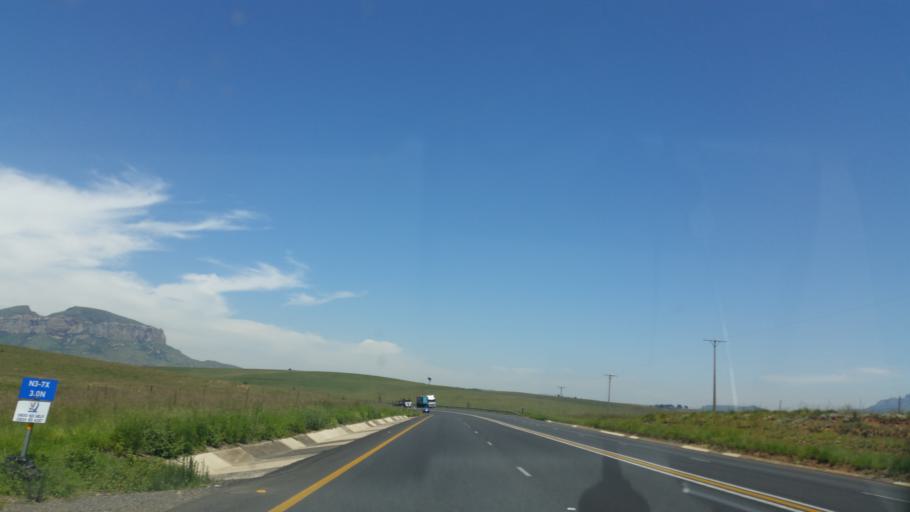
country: ZA
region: Orange Free State
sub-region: Thabo Mofutsanyana District Municipality
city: Harrismith
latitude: -28.3665
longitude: 29.3438
